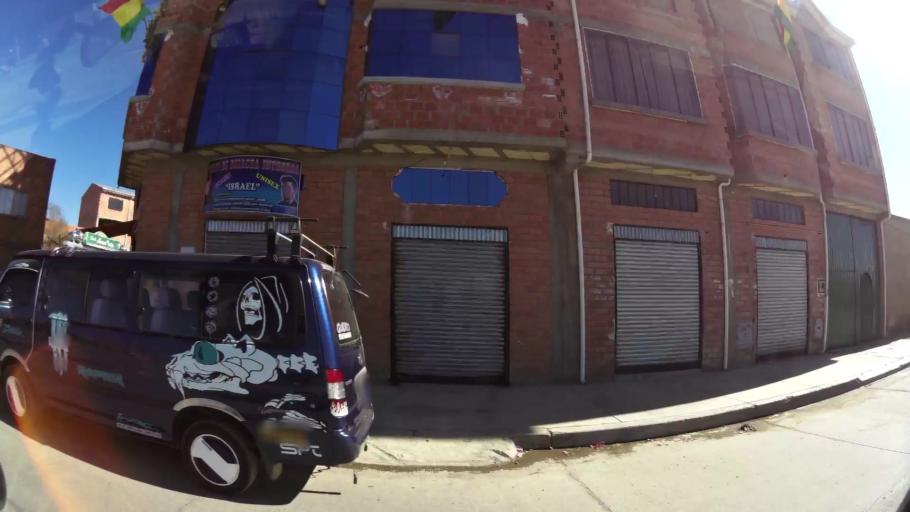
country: BO
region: La Paz
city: La Paz
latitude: -16.5312
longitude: -68.2218
